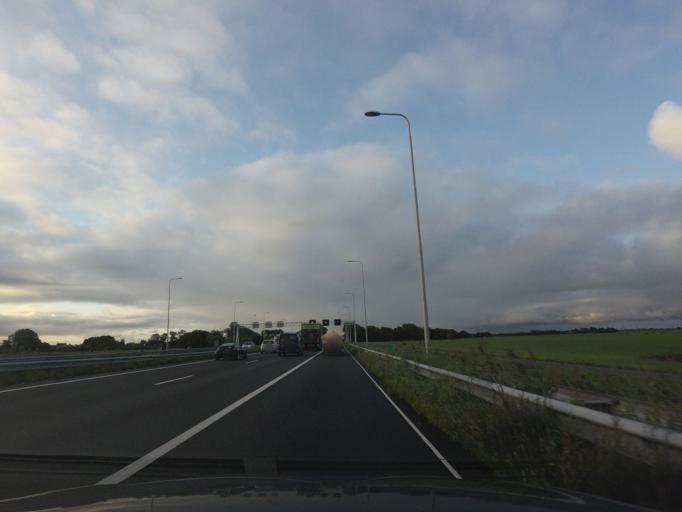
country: NL
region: North Holland
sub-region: Gemeente Uitgeest
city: Uitgeest
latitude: 52.5572
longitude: 4.7182
